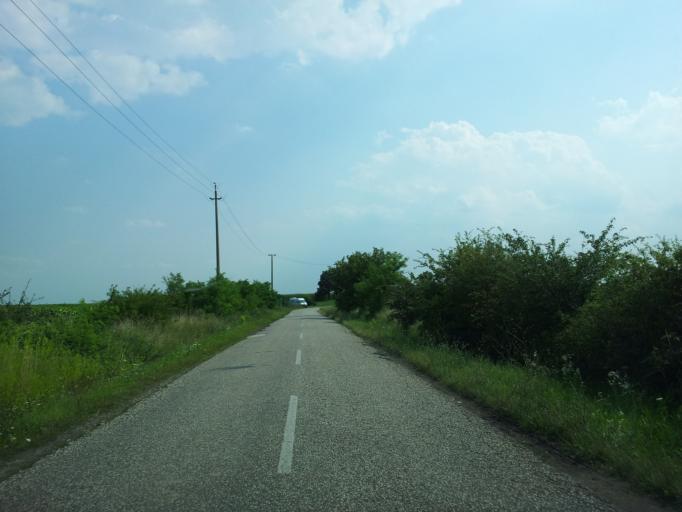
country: HU
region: Pest
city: Szigetujfalu
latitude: 47.2192
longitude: 18.9214
